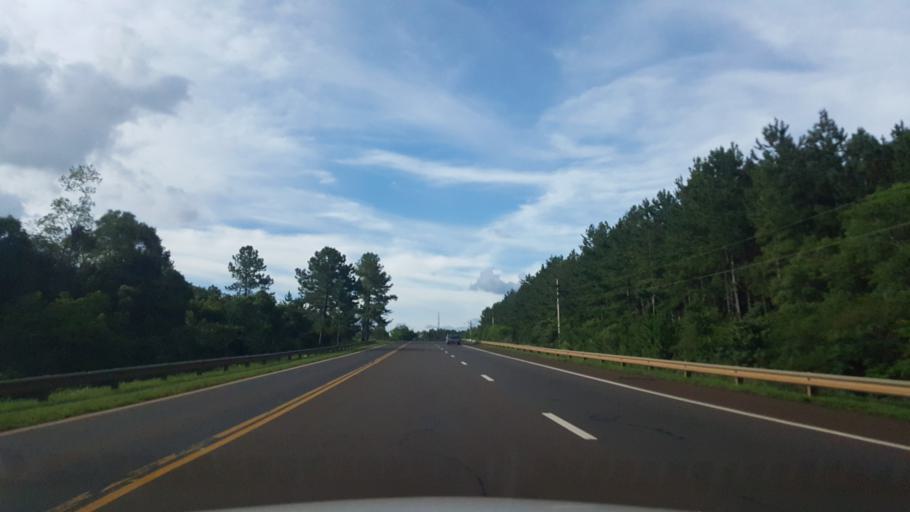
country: AR
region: Misiones
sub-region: Departamento de San Ignacio
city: San Ignacio
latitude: -27.2767
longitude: -55.5378
